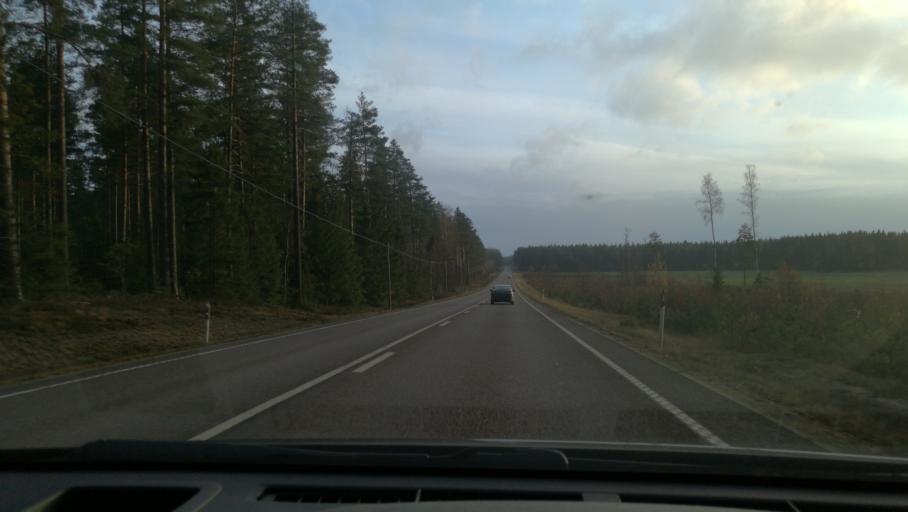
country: SE
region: Vaestmanland
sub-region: Kungsors Kommun
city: Kungsoer
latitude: 59.1979
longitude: 16.1036
